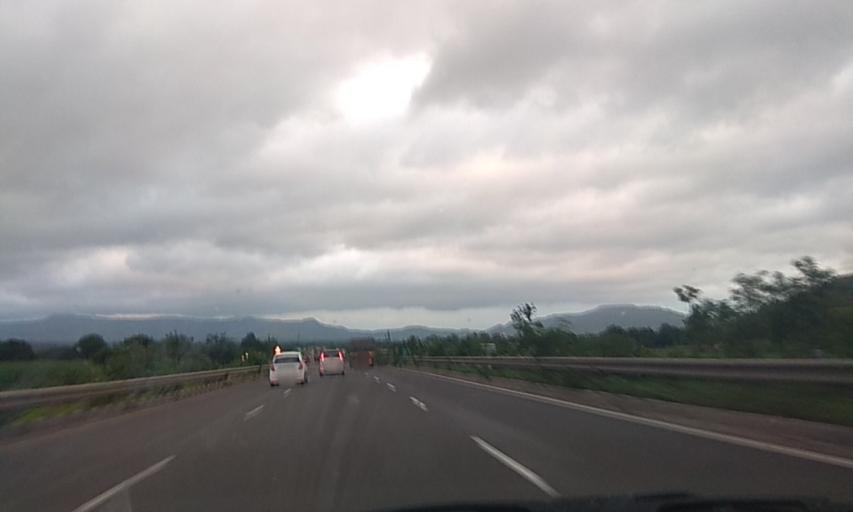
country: IN
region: Maharashtra
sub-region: Satara Division
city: Wai
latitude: 17.9315
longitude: 73.9761
